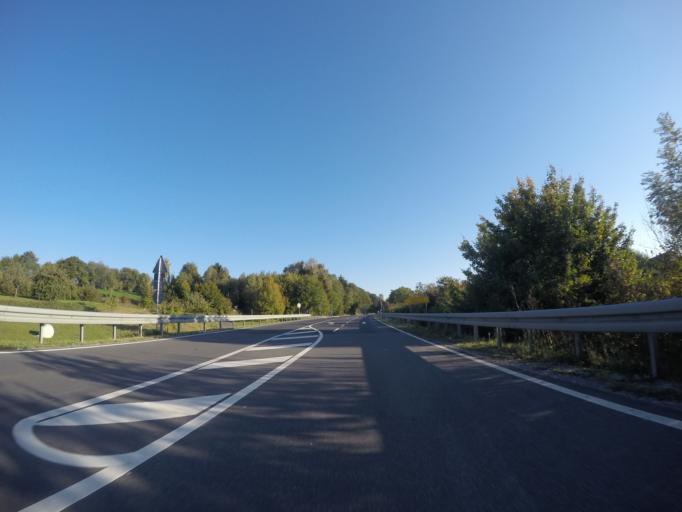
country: DE
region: Bavaria
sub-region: Regierungsbezirk Unterfranken
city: Kreuzwertheim
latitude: 49.7990
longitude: 9.5492
